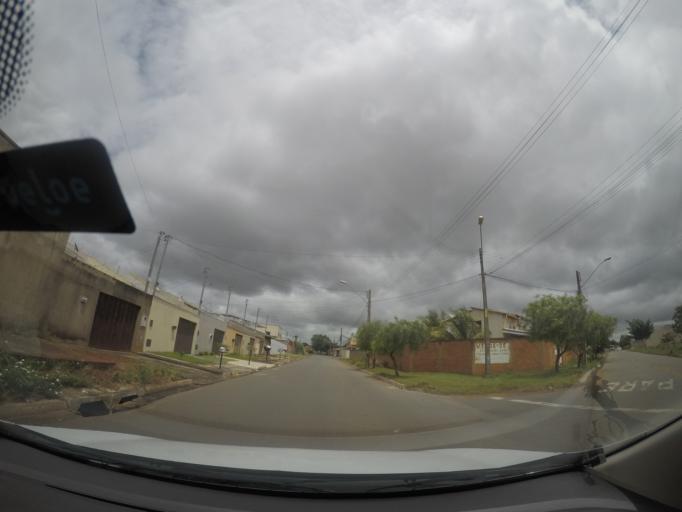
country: BR
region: Goias
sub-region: Goiania
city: Goiania
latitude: -16.7227
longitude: -49.3610
